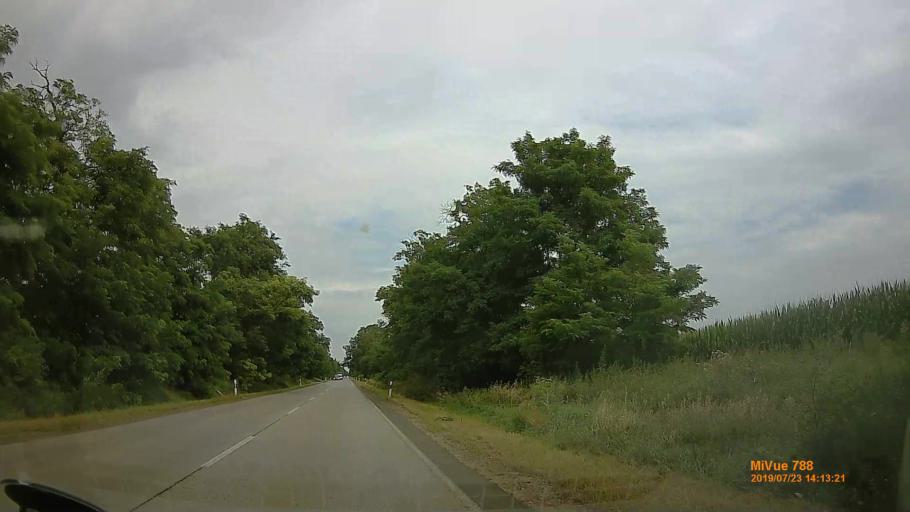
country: HU
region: Szabolcs-Szatmar-Bereg
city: Nagycserkesz
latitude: 47.9583
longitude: 21.4712
